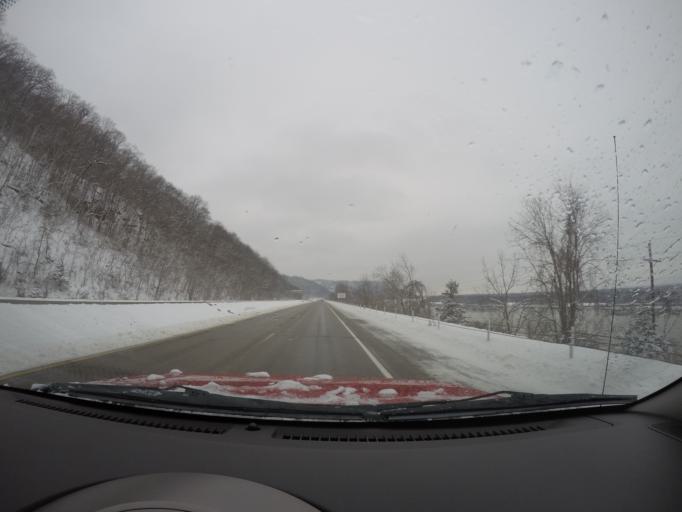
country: US
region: Minnesota
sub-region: Houston County
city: La Crescent
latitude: 43.8800
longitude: -91.3279
